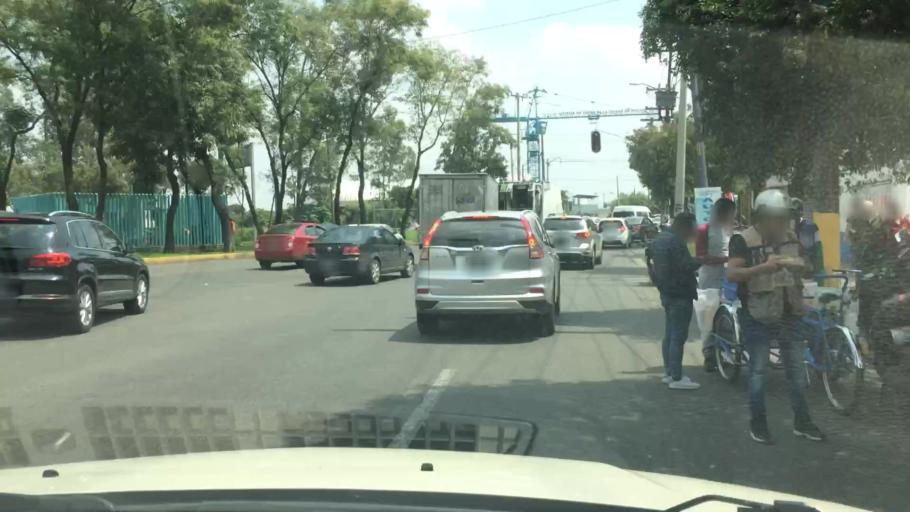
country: MX
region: Mexico City
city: Xochimilco
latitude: 19.2833
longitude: -99.1258
